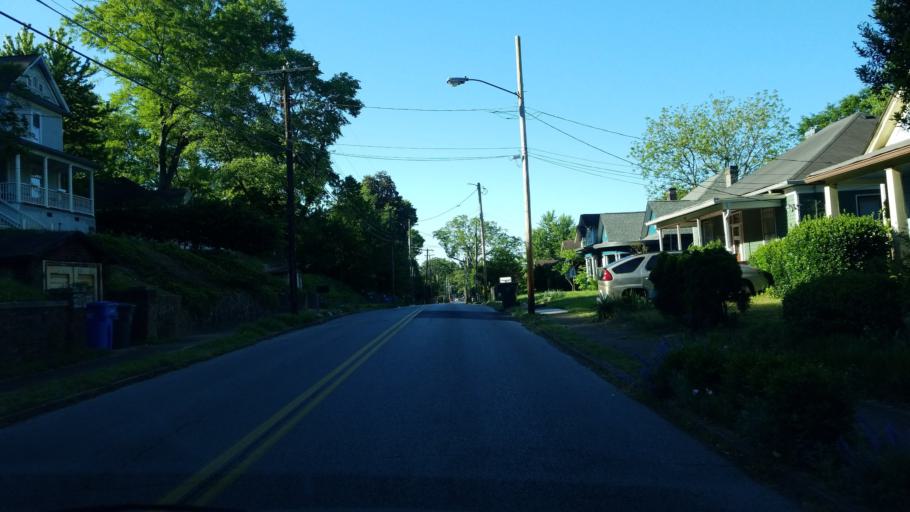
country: US
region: Tennessee
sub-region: Hamilton County
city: Lookout Mountain
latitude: 35.0016
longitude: -85.3276
